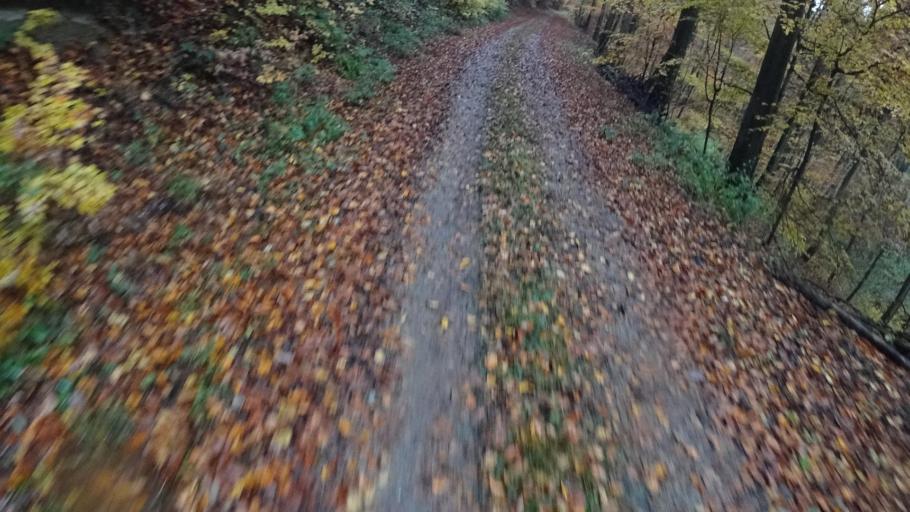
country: DE
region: Rheinland-Pfalz
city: Utzenhain
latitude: 50.1510
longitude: 7.6498
